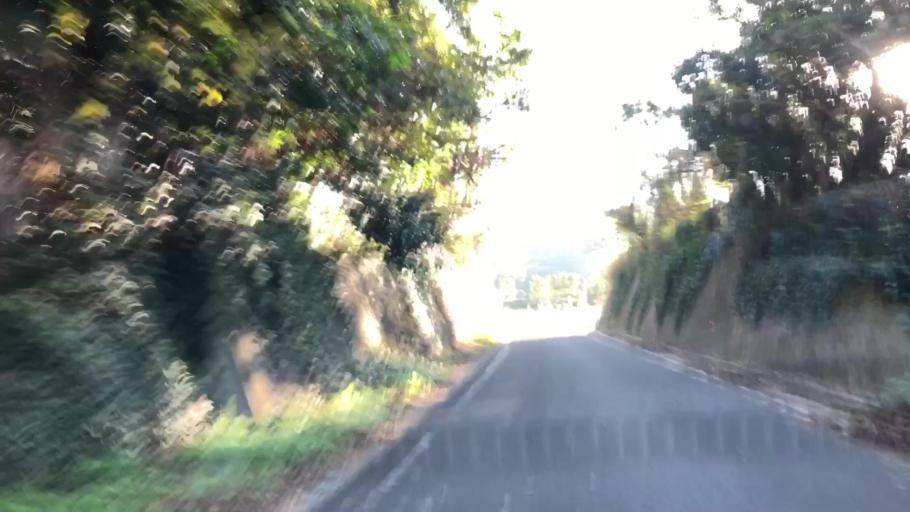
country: JP
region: Nagasaki
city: Sasebo
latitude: 33.0287
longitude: 129.6689
